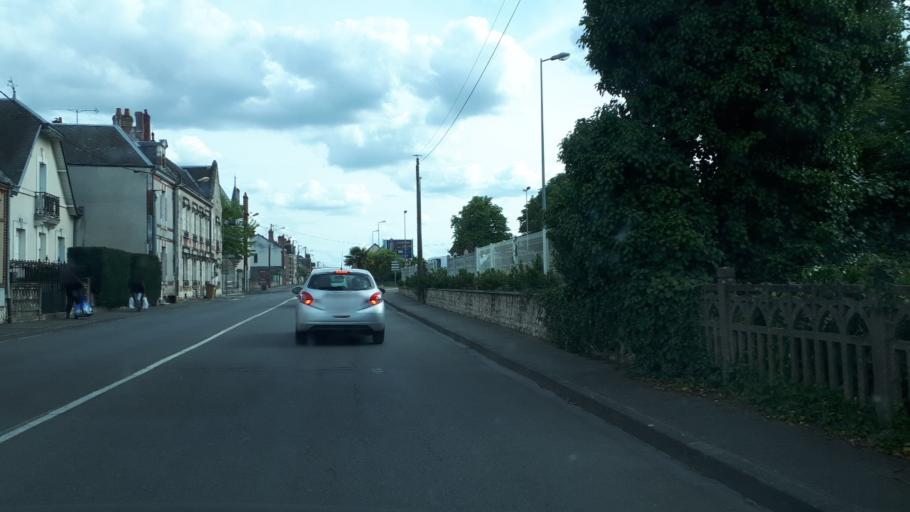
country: FR
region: Centre
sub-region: Departement du Loir-et-Cher
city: Romorantin-Lanthenay
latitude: 47.3561
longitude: 1.7398
